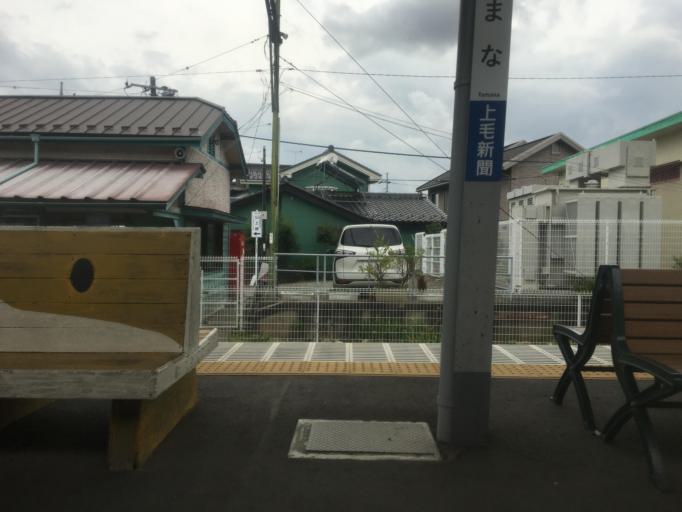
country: JP
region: Gunma
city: Fujioka
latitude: 36.2776
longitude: 139.0381
